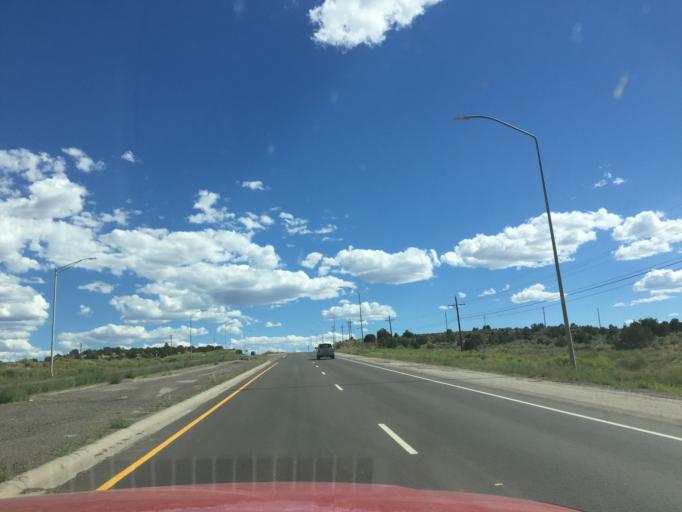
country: US
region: New Mexico
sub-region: McKinley County
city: Gallup
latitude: 35.5972
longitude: -108.7744
